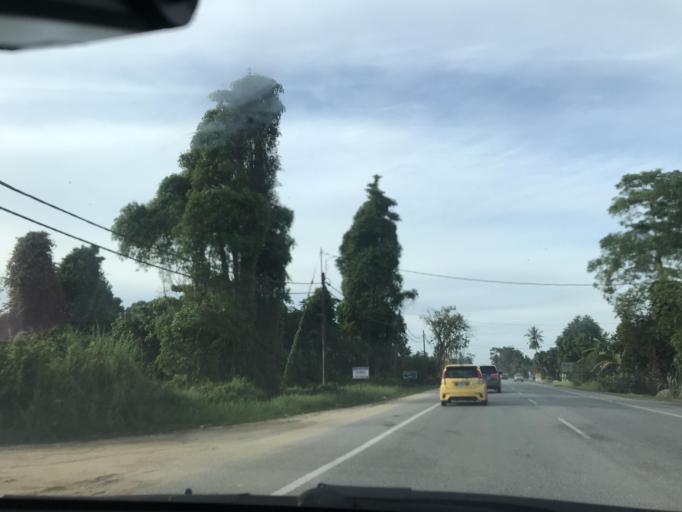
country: MY
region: Kelantan
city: Kampong Kadok
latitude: 5.9827
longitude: 102.1897
